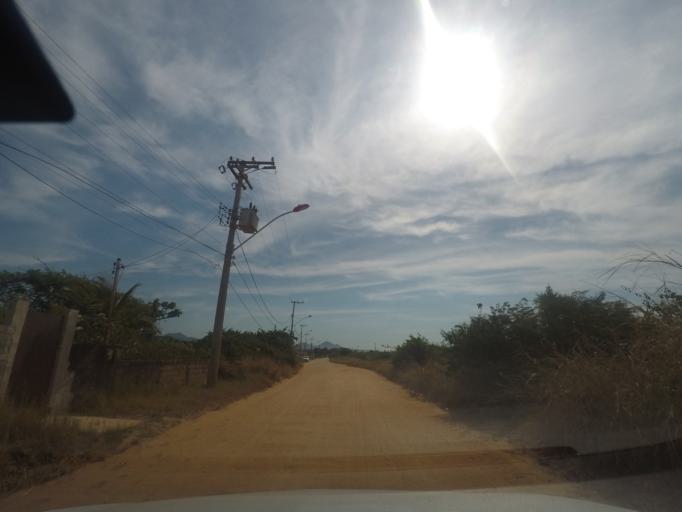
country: BR
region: Rio de Janeiro
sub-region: Marica
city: Marica
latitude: -22.9600
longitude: -42.8375
